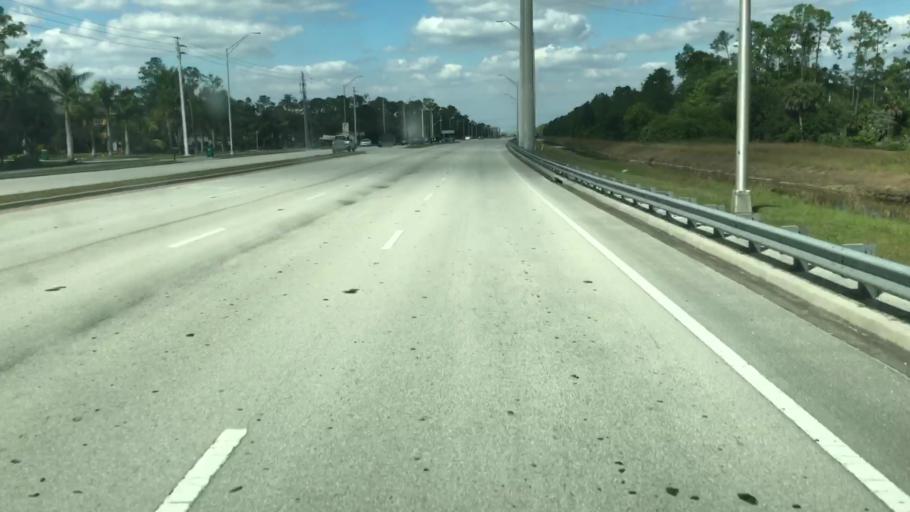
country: US
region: Florida
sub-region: Collier County
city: Vineyards
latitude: 26.2312
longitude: -81.6877
